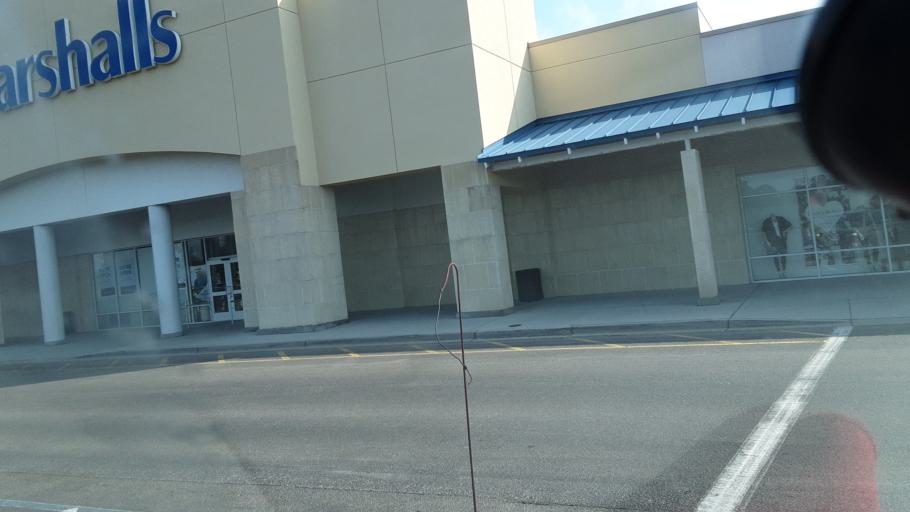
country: US
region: South Carolina
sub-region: Horry County
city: North Myrtle Beach
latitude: 33.7854
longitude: -78.7678
